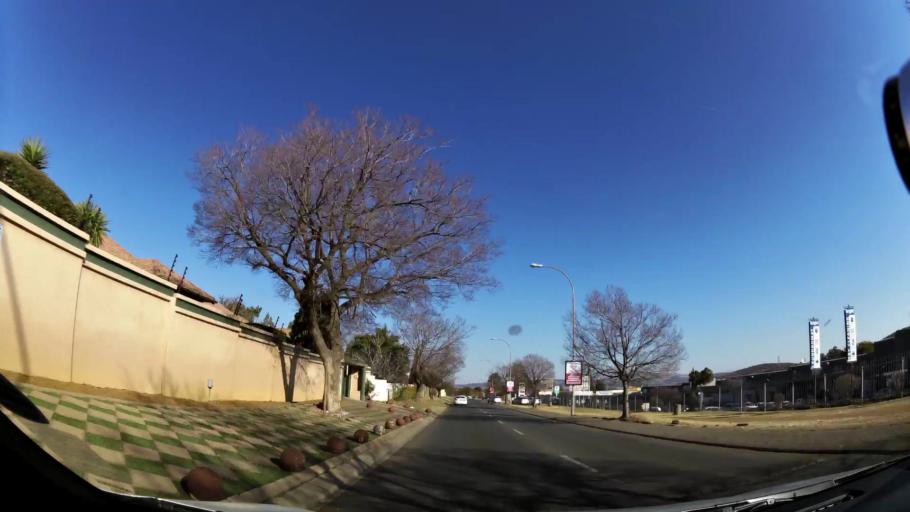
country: ZA
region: Gauteng
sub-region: City of Johannesburg Metropolitan Municipality
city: Johannesburg
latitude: -26.3004
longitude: 28.0538
